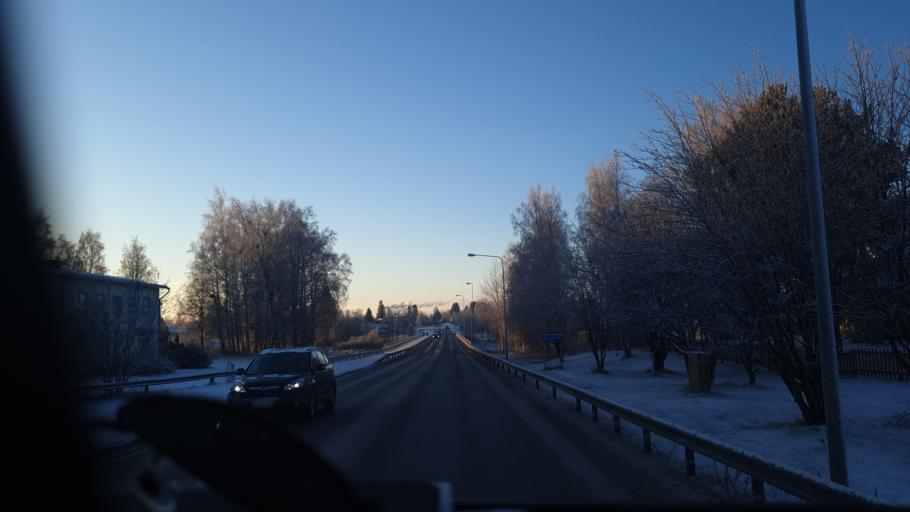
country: FI
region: Northern Ostrobothnia
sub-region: Ylivieska
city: Kalajoki
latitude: 64.2591
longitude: 23.9439
